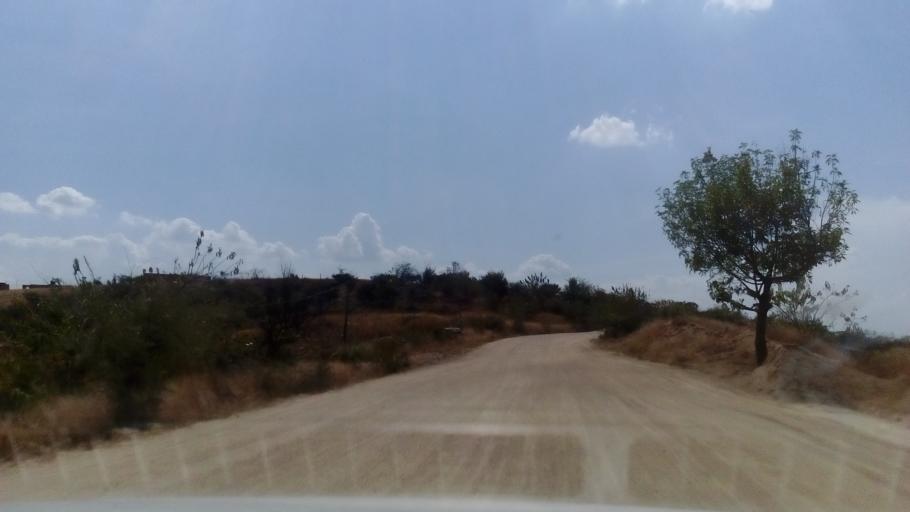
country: MX
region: Guanajuato
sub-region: Silao de la Victoria
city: Loma de Yerbabuena
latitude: 21.0865
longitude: -101.4436
